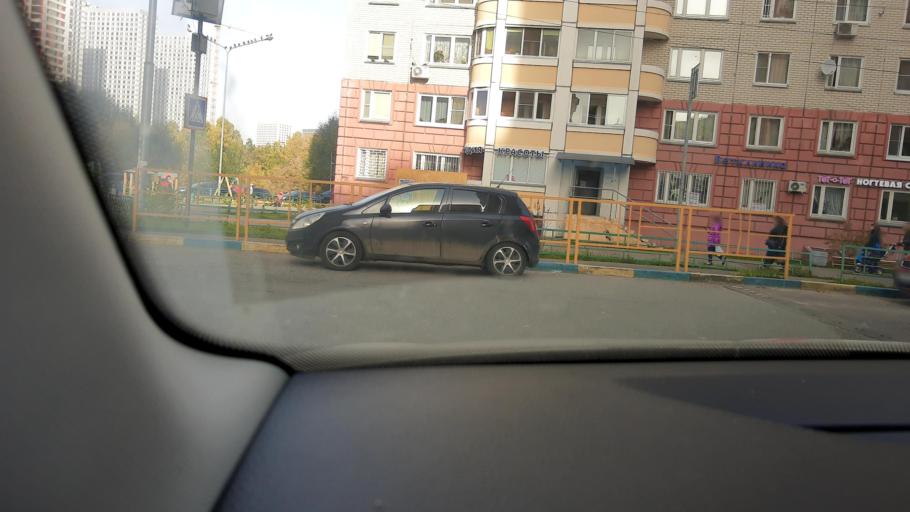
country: RU
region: Moscow
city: Zhulebino
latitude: 55.6682
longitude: 37.8582
